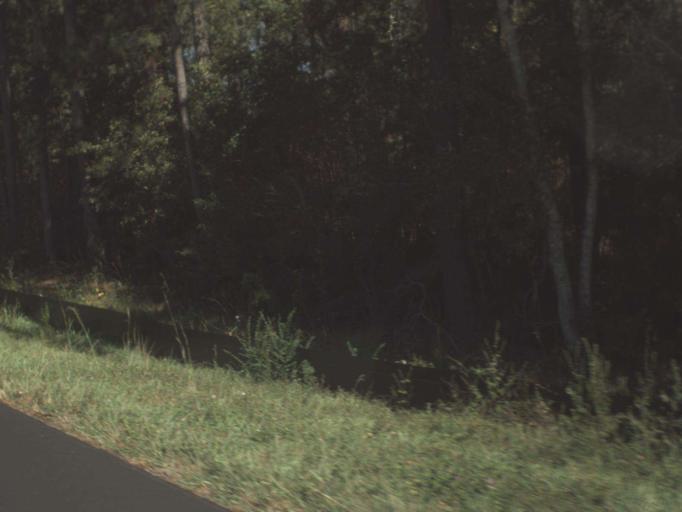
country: US
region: Alabama
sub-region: Covington County
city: Florala
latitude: 30.8961
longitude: -86.2813
